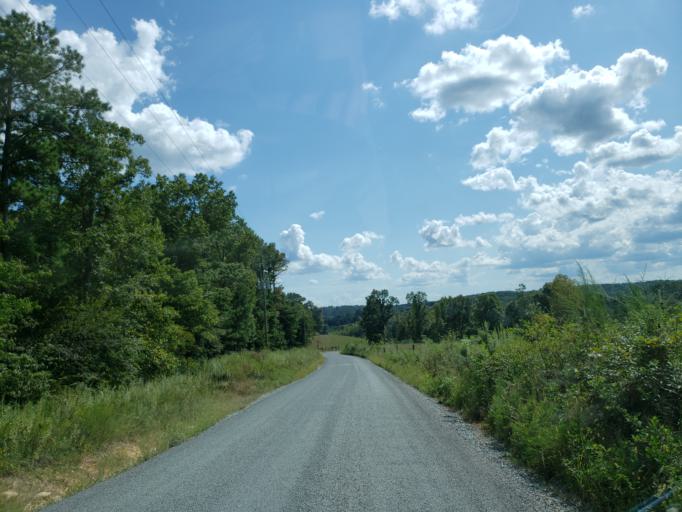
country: US
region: Georgia
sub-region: Pickens County
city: Jasper
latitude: 34.4255
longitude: -84.4553
